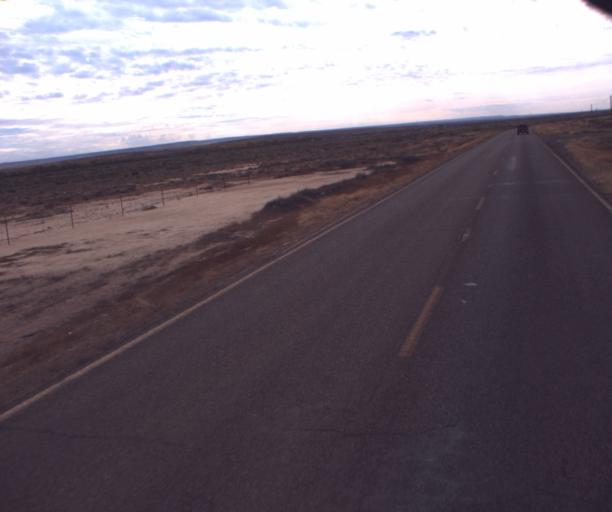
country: US
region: Arizona
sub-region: Apache County
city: Many Farms
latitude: 36.3105
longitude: -109.6106
